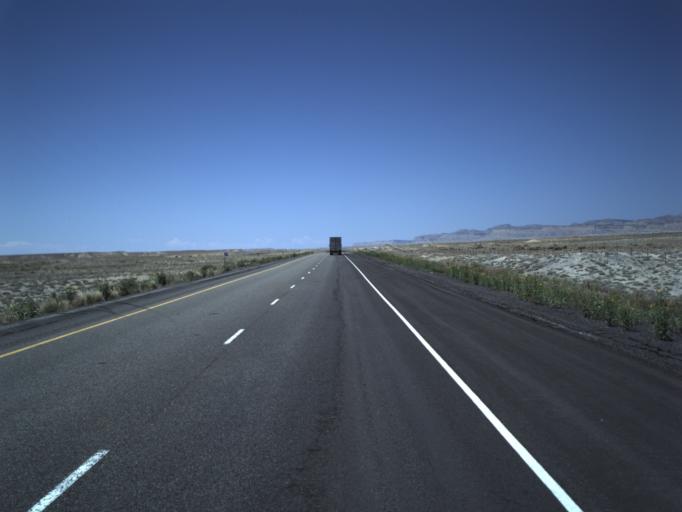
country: US
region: Utah
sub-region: Grand County
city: Moab
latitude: 38.9372
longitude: -109.4750
